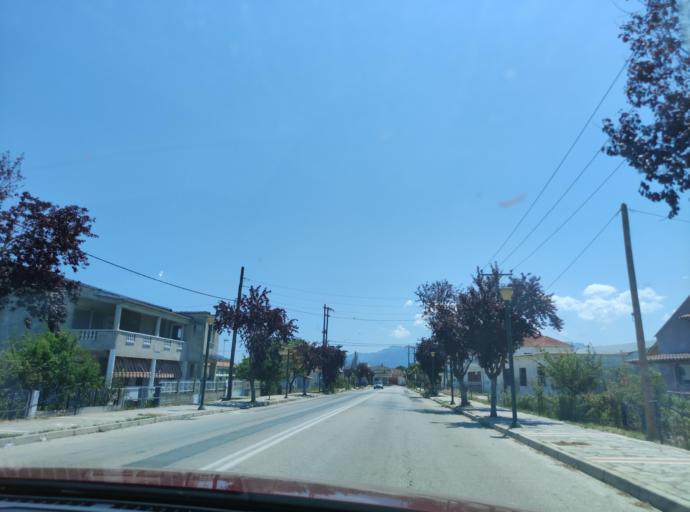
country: GR
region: East Macedonia and Thrace
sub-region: Nomos Kavalas
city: Keramoti
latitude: 40.8615
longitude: 24.7057
